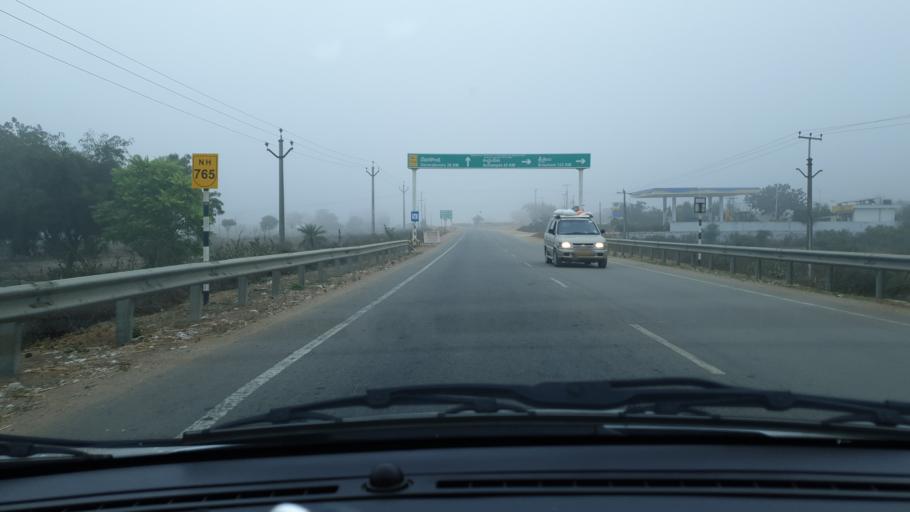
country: IN
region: Telangana
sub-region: Mahbubnagar
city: Nagar Karnul
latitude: 16.6620
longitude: 78.5743
